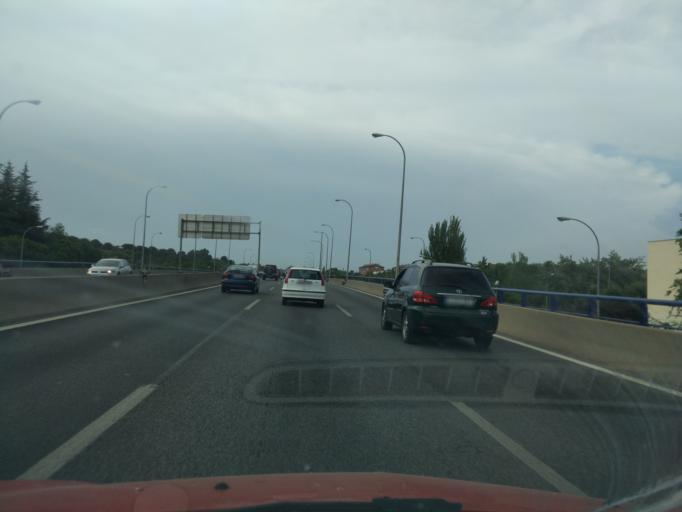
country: ES
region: Madrid
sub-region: Provincia de Madrid
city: Carabanchel
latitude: 40.3723
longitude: -3.7198
